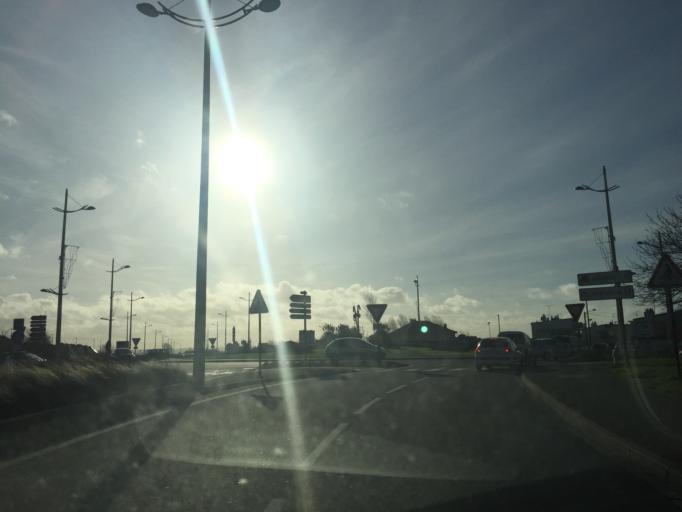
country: FR
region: Nord-Pas-de-Calais
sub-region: Departement du Pas-de-Calais
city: Calais
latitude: 50.9466
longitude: 1.8381
